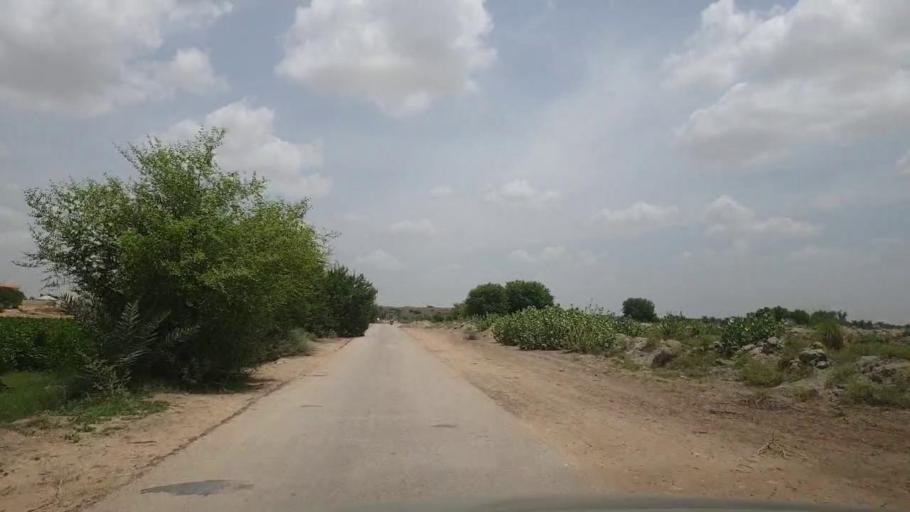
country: PK
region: Sindh
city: Kot Diji
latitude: 27.2007
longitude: 69.0606
